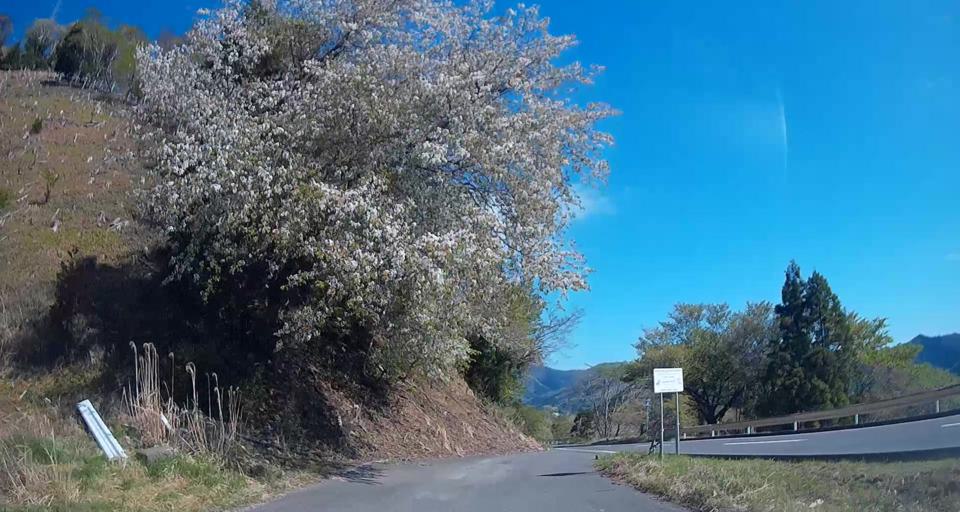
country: JP
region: Miyagi
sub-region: Oshika Gun
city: Onagawa Cho
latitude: 38.4312
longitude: 141.4475
